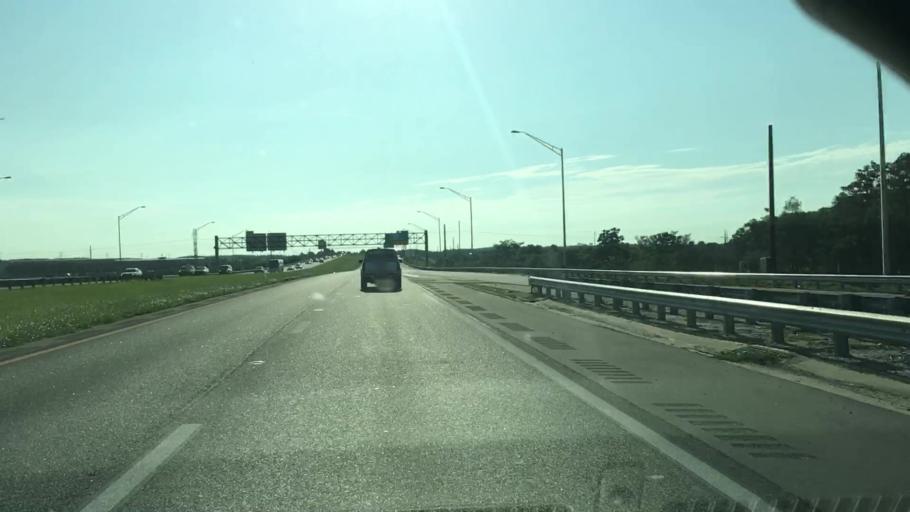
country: US
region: Florida
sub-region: Orange County
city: Meadow Woods
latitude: 28.3681
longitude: -81.3810
